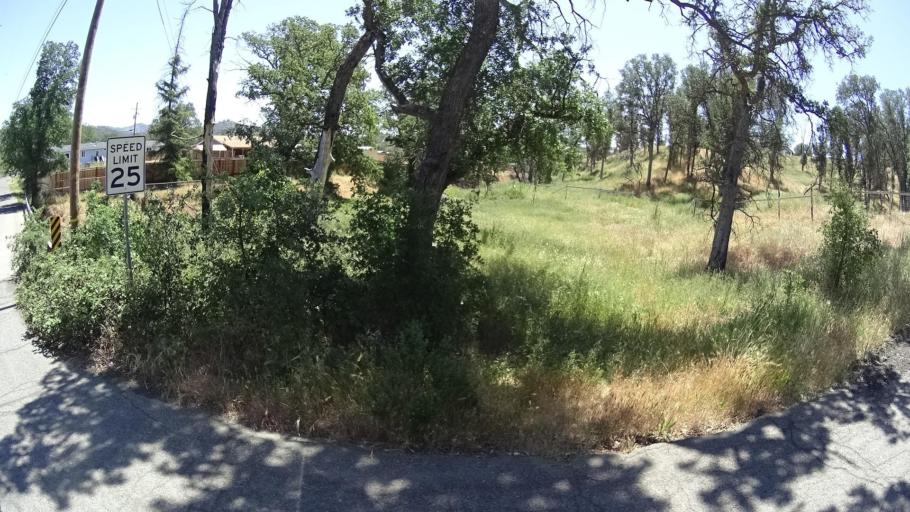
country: US
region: California
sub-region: Lake County
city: Lower Lake
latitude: 38.9142
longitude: -122.5939
